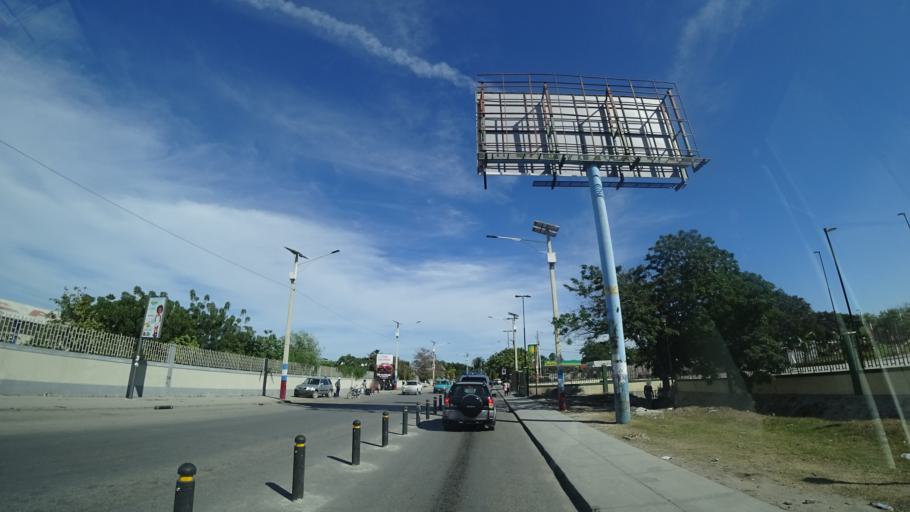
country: HT
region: Ouest
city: Delmas 73
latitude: 18.5751
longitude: -72.2985
